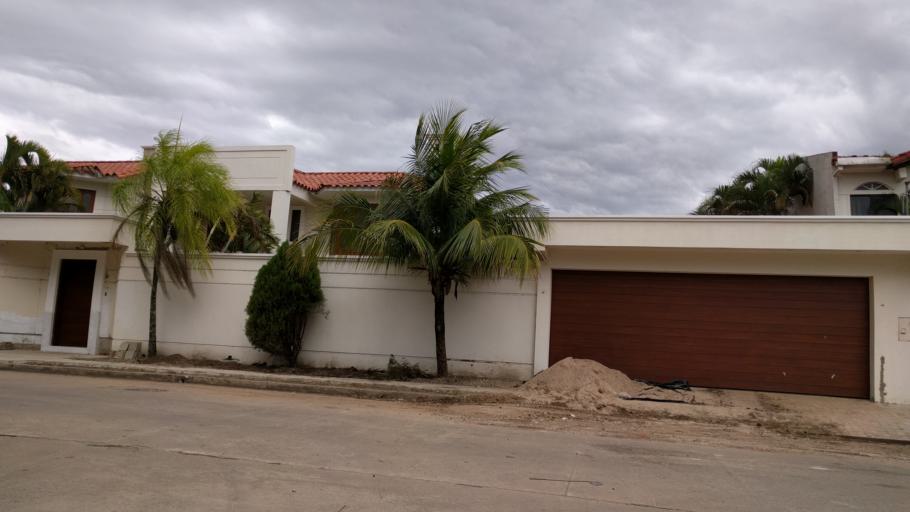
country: BO
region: Santa Cruz
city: Santa Cruz de la Sierra
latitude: -17.8018
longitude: -63.2135
